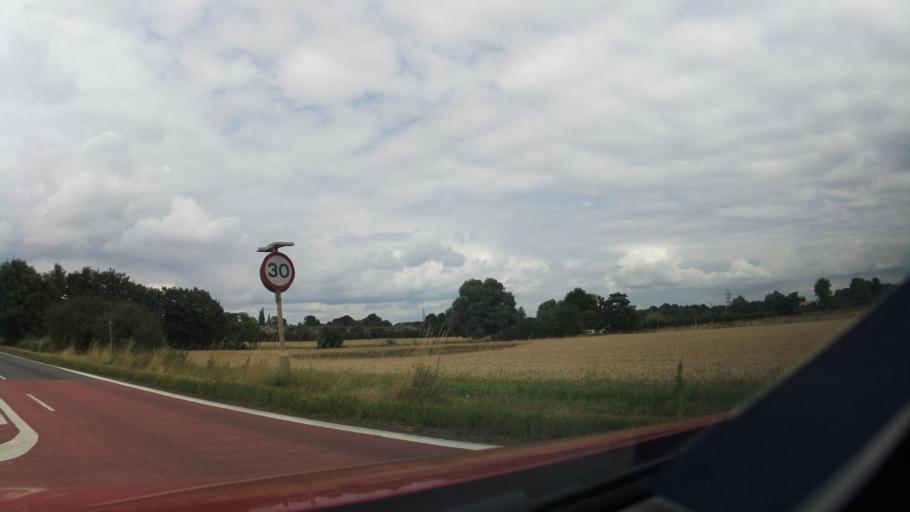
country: GB
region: England
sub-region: District of Rutland
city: Ryhall
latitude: 52.6772
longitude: -0.4710
